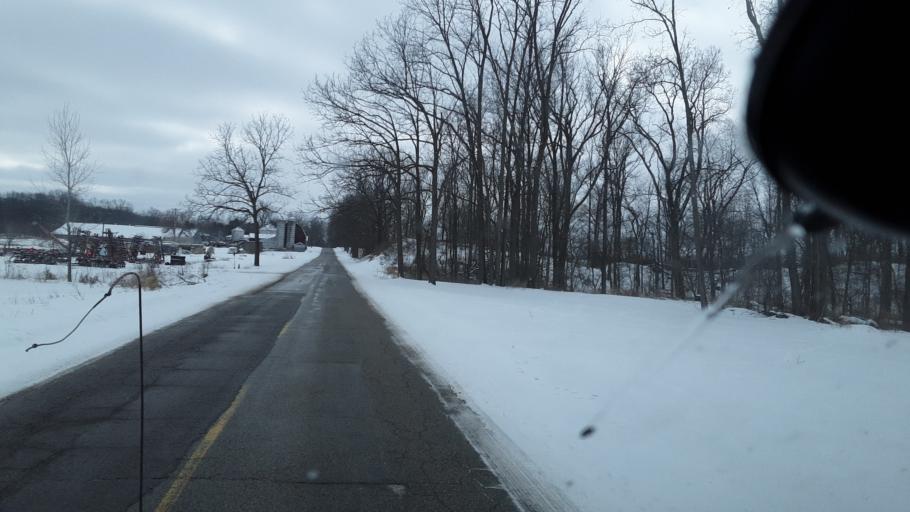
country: US
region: Michigan
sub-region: Ingham County
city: Mason
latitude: 42.5329
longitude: -84.3889
